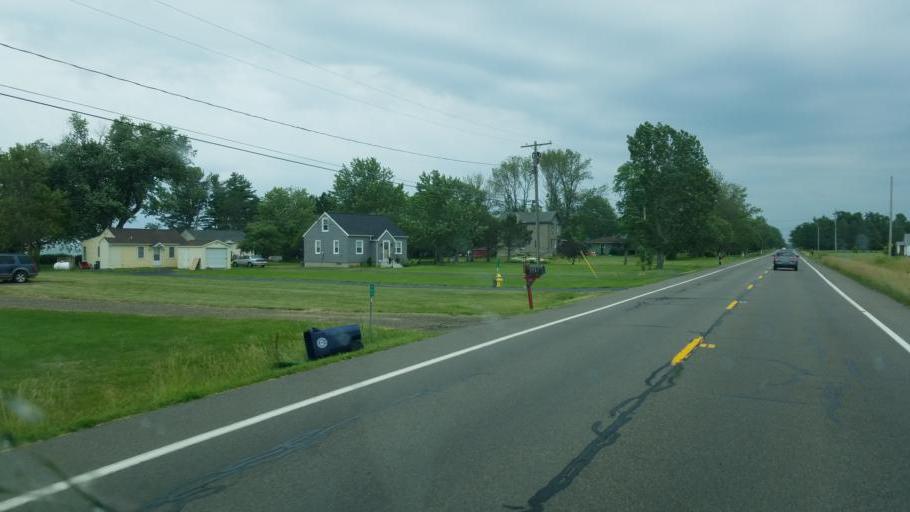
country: US
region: New York
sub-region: Niagara County
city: Ransomville
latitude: 43.2998
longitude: -78.8969
